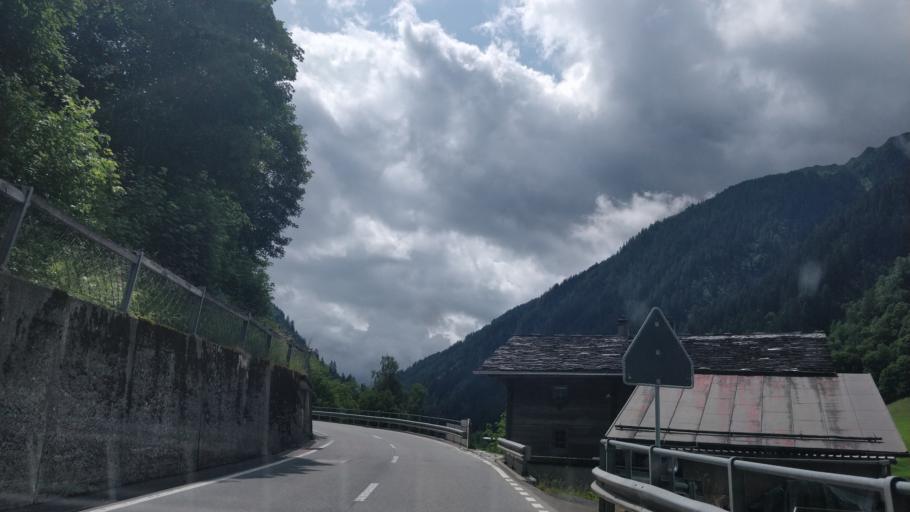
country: CH
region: Grisons
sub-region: Surselva District
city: Ilanz
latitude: 46.6600
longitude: 9.1899
